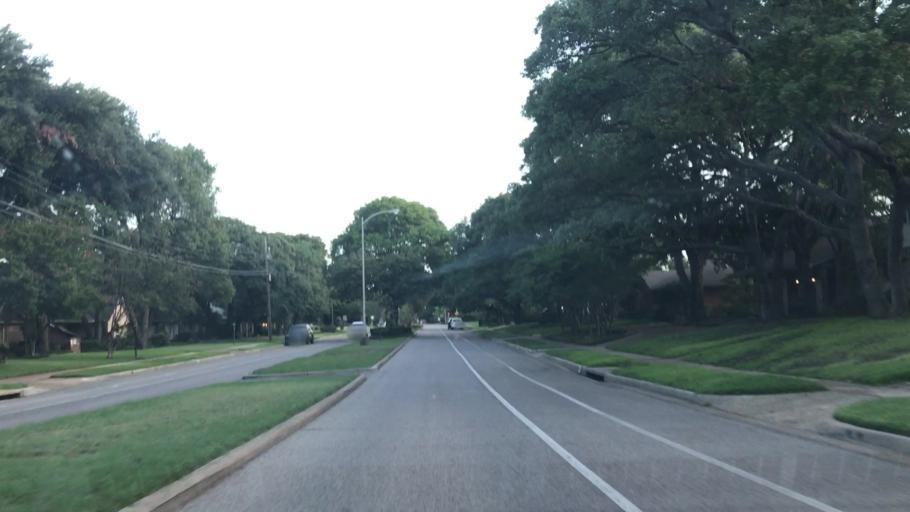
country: US
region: Texas
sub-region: Dallas County
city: Richardson
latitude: 32.9537
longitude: -96.7561
